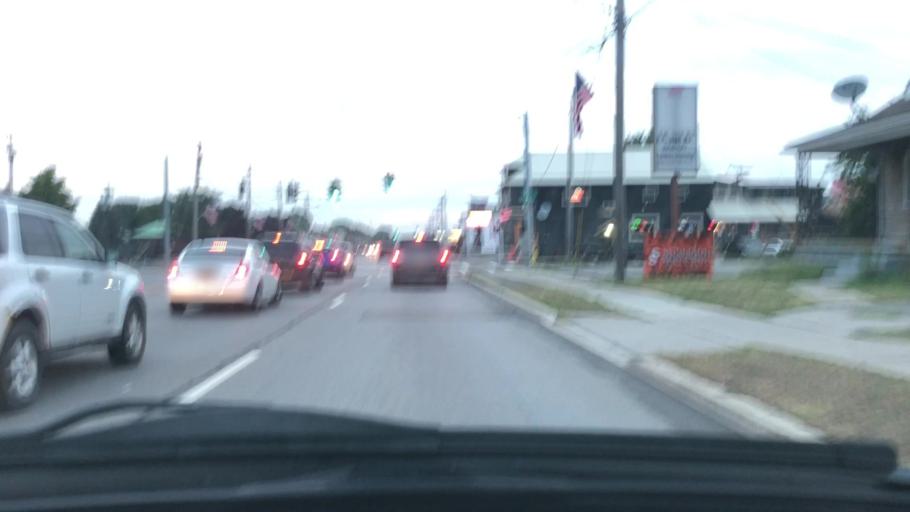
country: US
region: New York
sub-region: Erie County
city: Sloan
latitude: 42.9168
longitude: -78.7842
